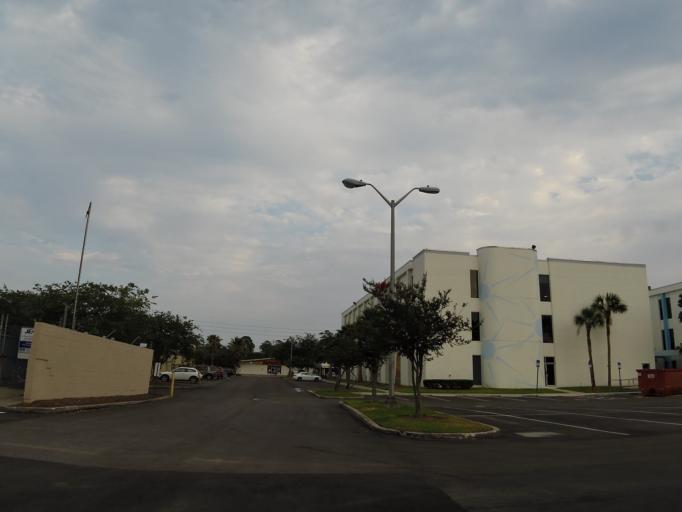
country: US
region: Florida
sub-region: Duval County
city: Jacksonville
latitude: 30.2636
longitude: -81.6247
